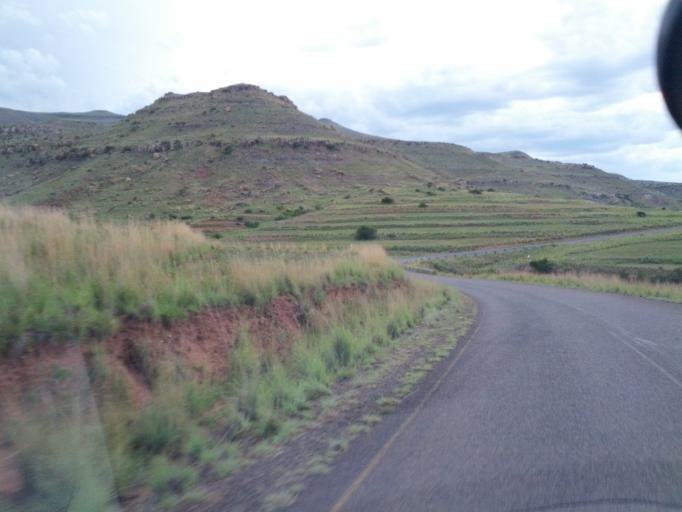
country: LS
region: Qacha's Nek
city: Qacha's Nek
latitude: -30.0668
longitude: 28.5505
